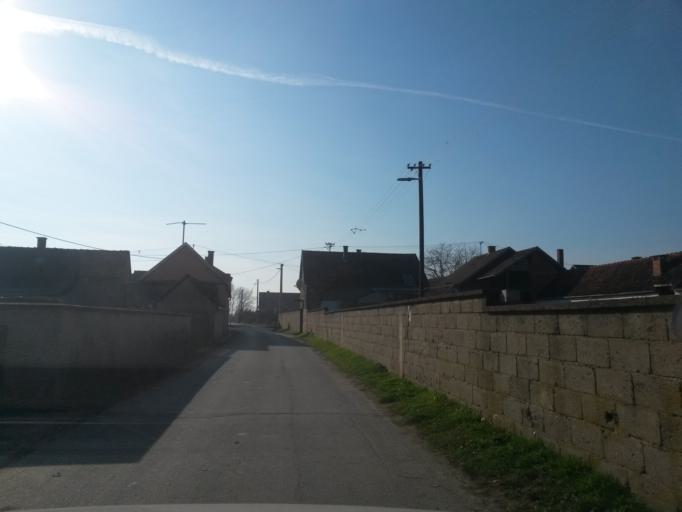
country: HR
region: Vukovarsko-Srijemska
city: Privlaka
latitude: 45.1957
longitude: 18.8353
